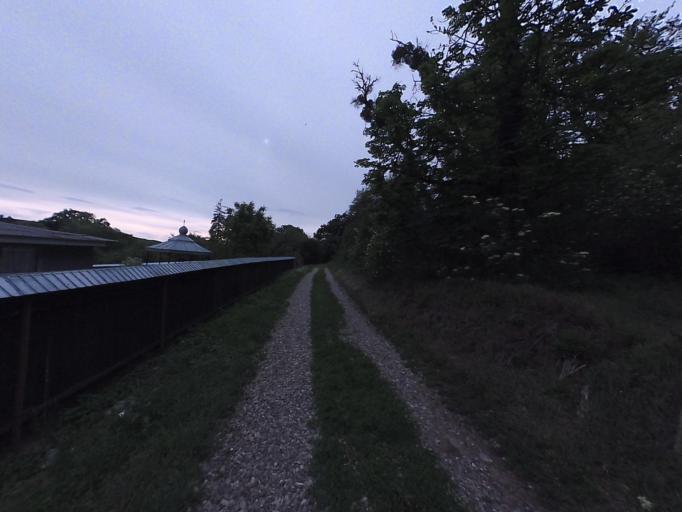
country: RO
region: Neamt
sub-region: Comuna Dulcesti
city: Dulcesti
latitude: 46.9671
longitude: 26.7854
